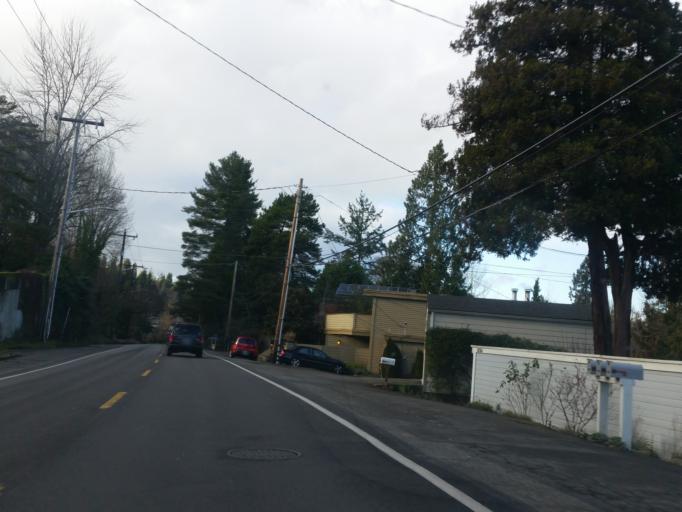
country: US
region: Washington
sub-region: King County
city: Inglewood-Finn Hill
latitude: 47.6929
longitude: -122.2712
